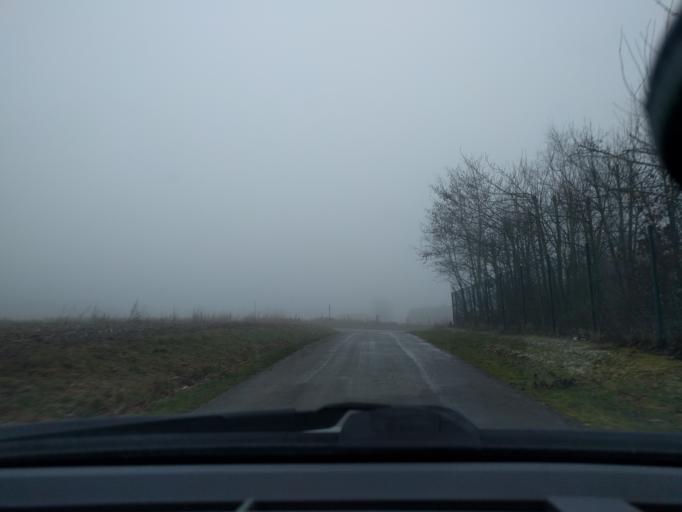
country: BE
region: Wallonia
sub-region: Province du Luxembourg
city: Gouvy
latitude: 50.1923
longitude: 5.9570
